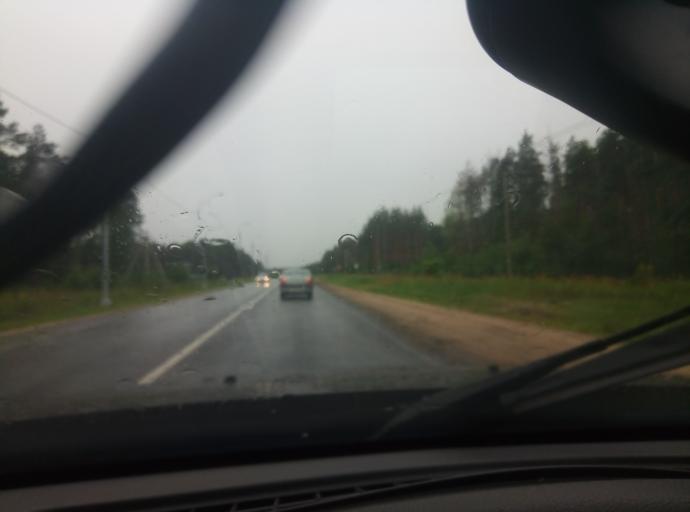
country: RU
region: Moskovskaya
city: Protvino
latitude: 54.8839
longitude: 37.2690
